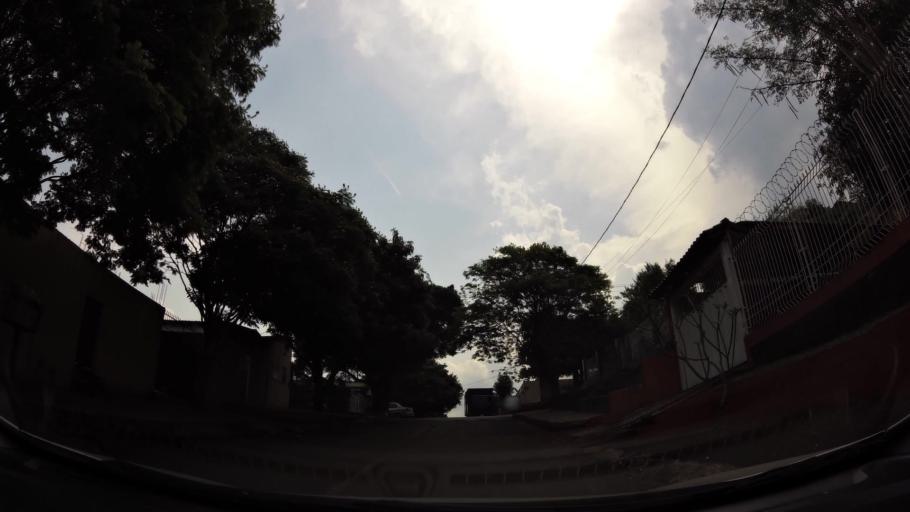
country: PY
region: Alto Parana
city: Presidente Franco
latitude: -25.5459
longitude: -54.6092
